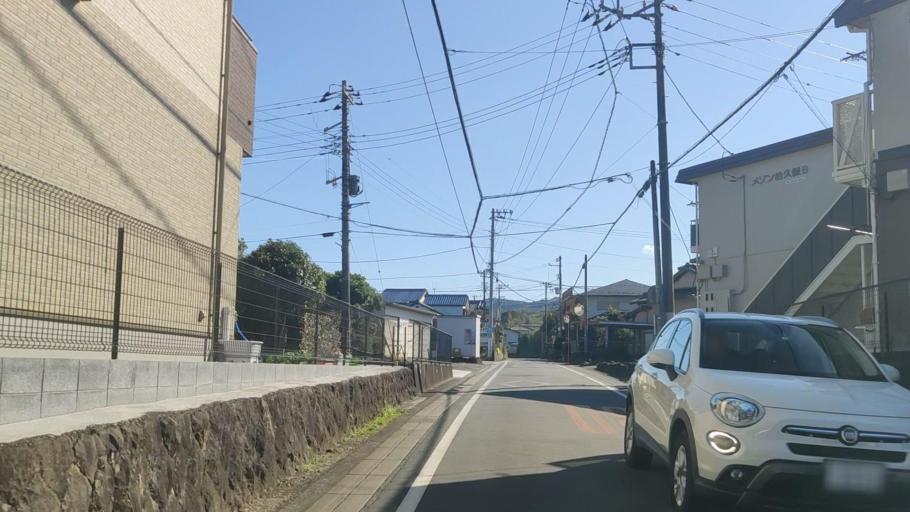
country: JP
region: Shizuoka
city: Ito
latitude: 34.9771
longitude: 138.9522
